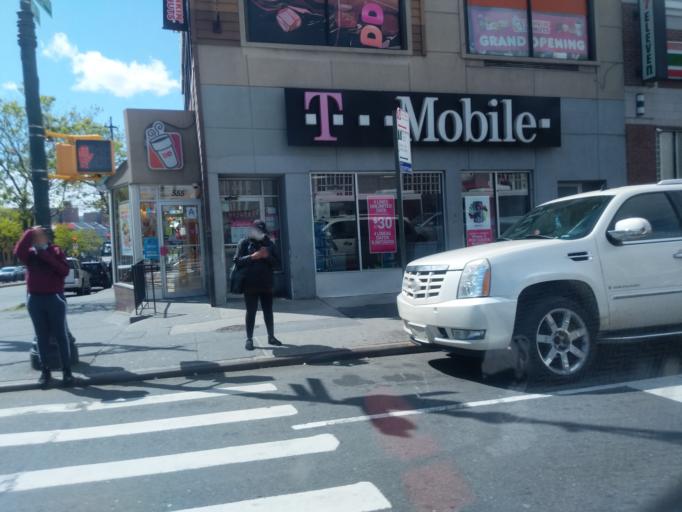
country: US
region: New York
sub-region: New York County
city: Inwood
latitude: 40.8187
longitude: -73.9273
